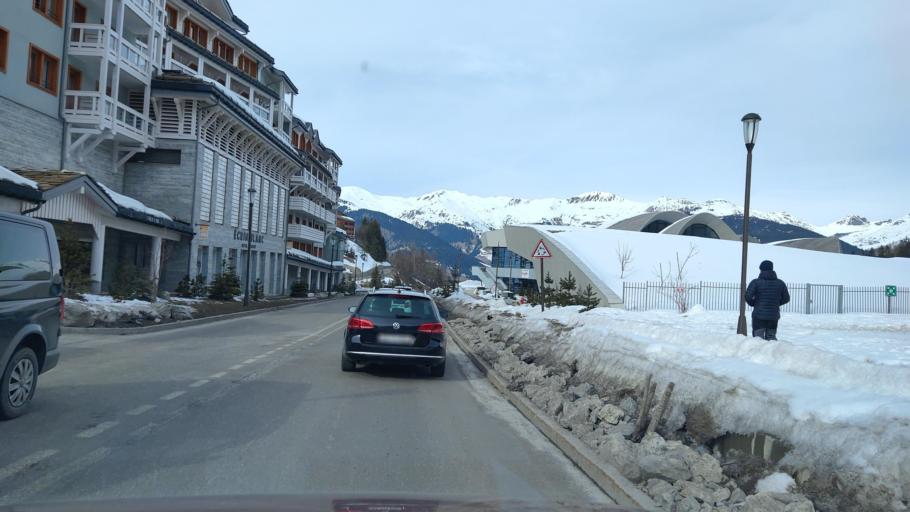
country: FR
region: Rhone-Alpes
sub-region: Departement de la Savoie
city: Courchevel
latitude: 45.4156
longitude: 6.6466
